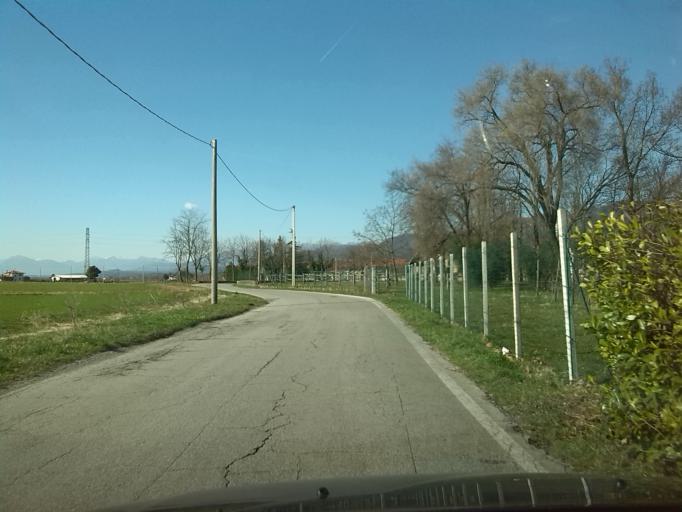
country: IT
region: Friuli Venezia Giulia
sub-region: Provincia di Udine
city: Cividale del Friuli
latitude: 46.0964
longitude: 13.4164
